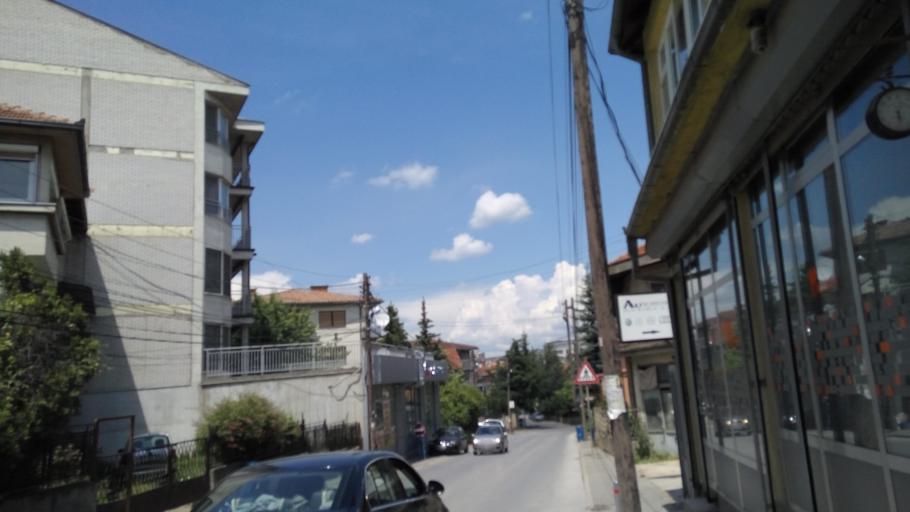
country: XK
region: Pristina
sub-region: Komuna e Prishtines
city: Pristina
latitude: 42.6626
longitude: 21.1528
